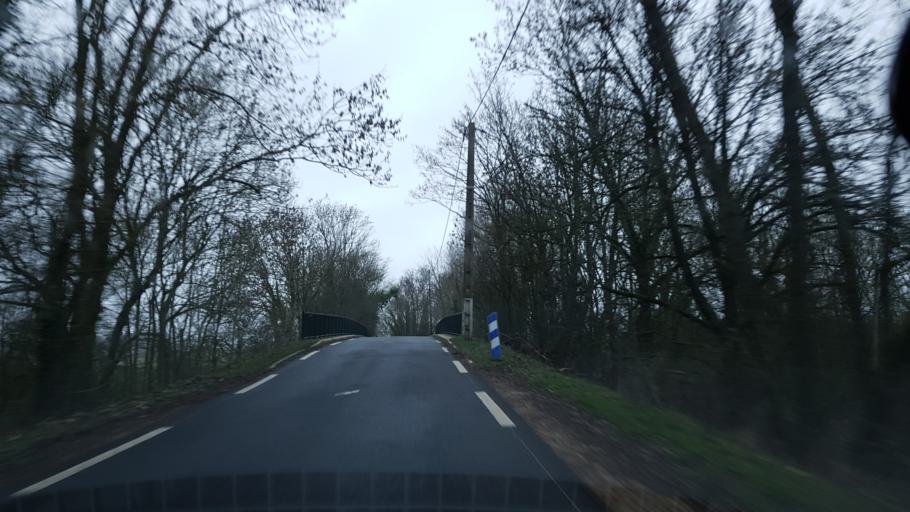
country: FR
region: Ile-de-France
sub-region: Departement de l'Essonne
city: Limours
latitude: 48.6593
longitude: 2.0931
